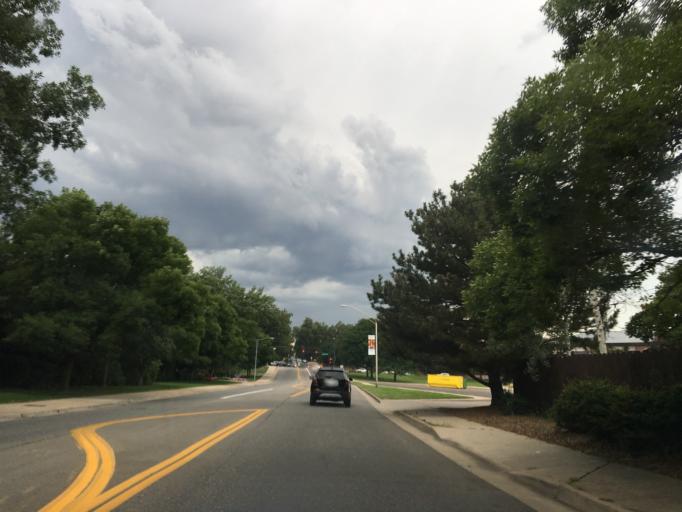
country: US
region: Colorado
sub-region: Arapahoe County
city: Glendale
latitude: 39.7111
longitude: -104.9565
